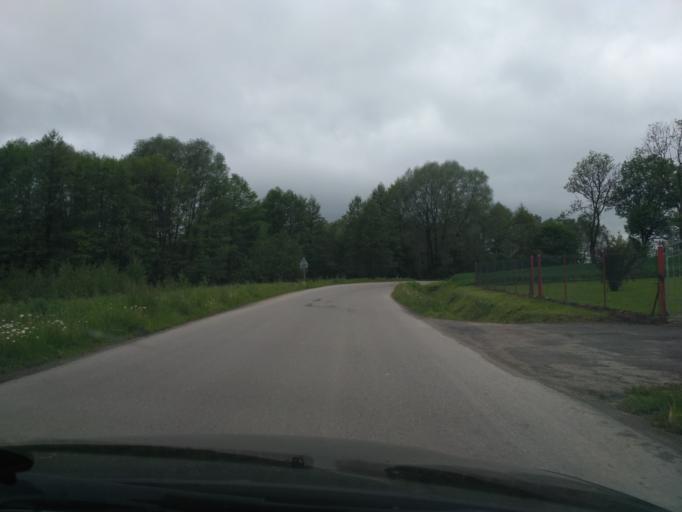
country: PL
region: Subcarpathian Voivodeship
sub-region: Powiat strzyzowski
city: Frysztak
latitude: 49.8045
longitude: 21.5565
